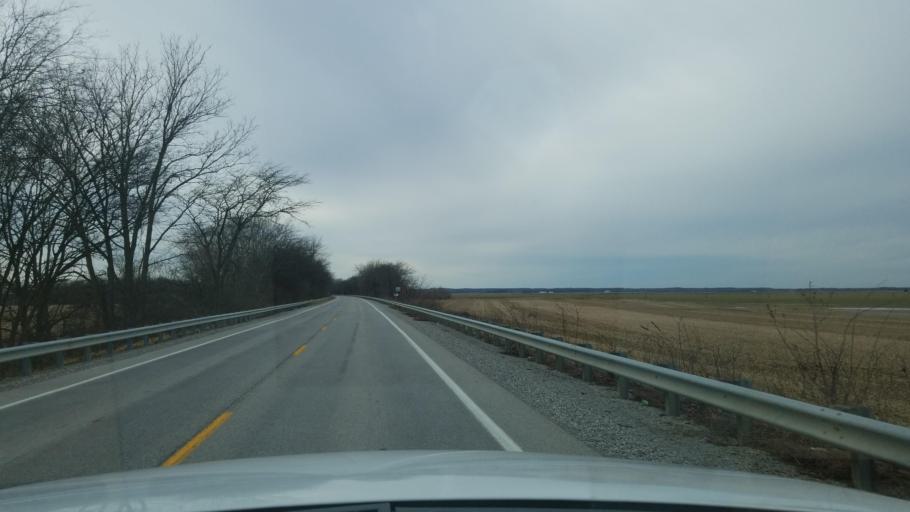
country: US
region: Indiana
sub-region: Posey County
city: Mount Vernon
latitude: 37.9429
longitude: -88.0541
